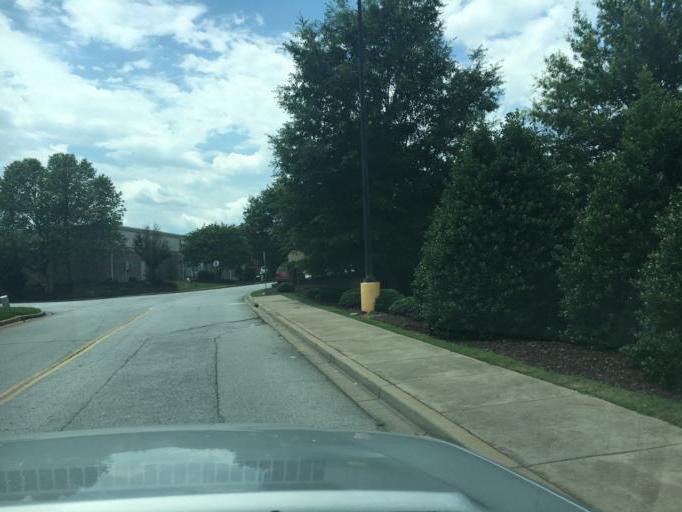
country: US
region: South Carolina
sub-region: Greenville County
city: Five Forks
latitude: 34.8609
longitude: -82.2639
